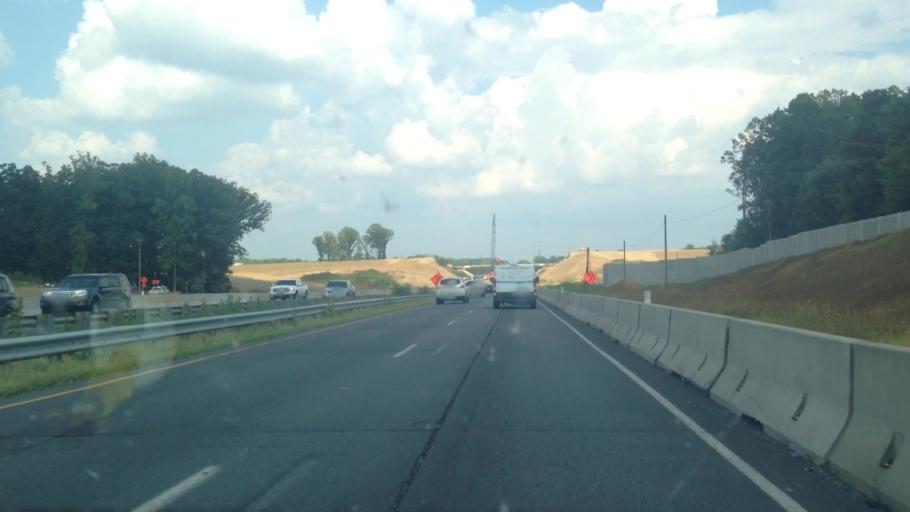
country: US
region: North Carolina
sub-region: Forsyth County
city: Walkertown
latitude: 36.1132
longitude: -80.1386
